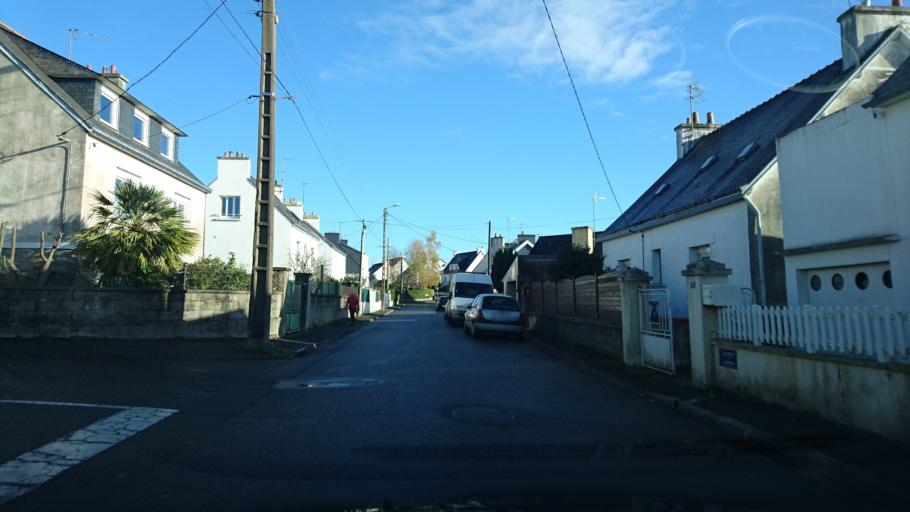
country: FR
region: Brittany
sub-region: Departement du Finistere
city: Quimperle
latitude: 47.8734
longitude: -3.5602
